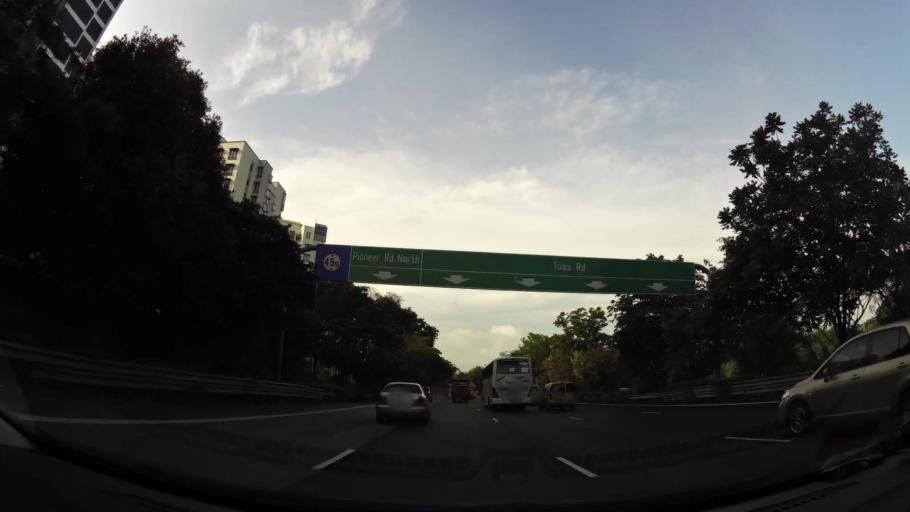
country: MY
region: Johor
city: Johor Bahru
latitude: 1.3521
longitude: 103.6958
